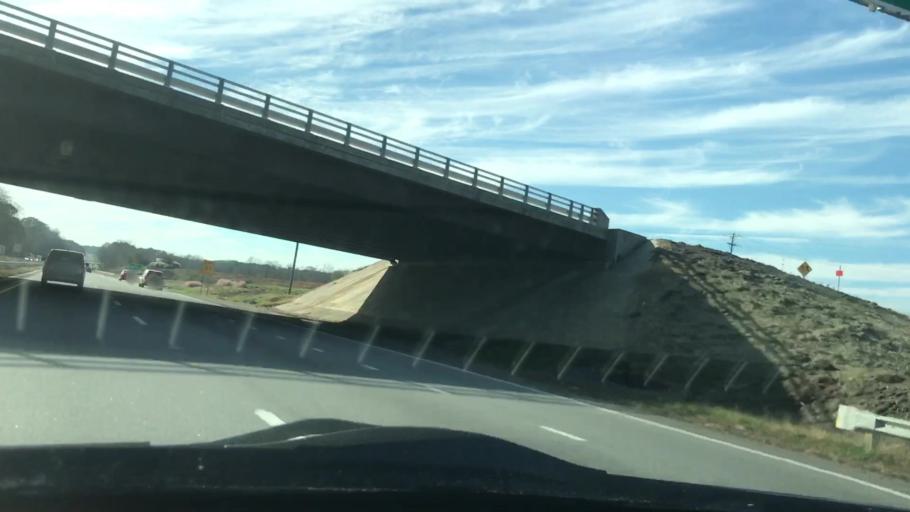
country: US
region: North Carolina
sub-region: Davie County
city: Bermuda Run
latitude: 36.0073
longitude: -80.4415
